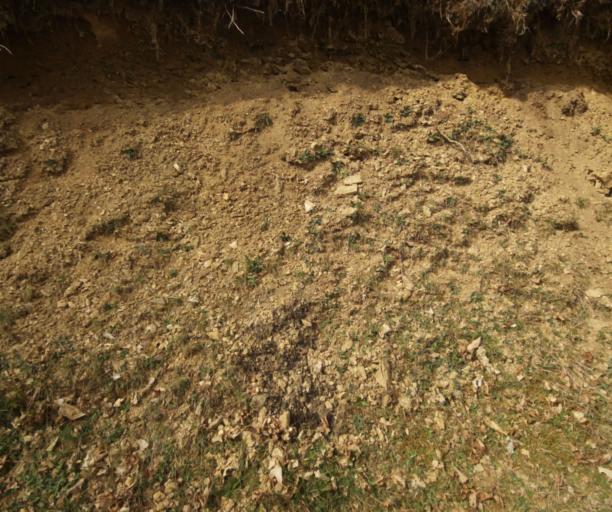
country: FR
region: Limousin
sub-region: Departement de la Correze
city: Naves
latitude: 45.3197
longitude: 1.7879
